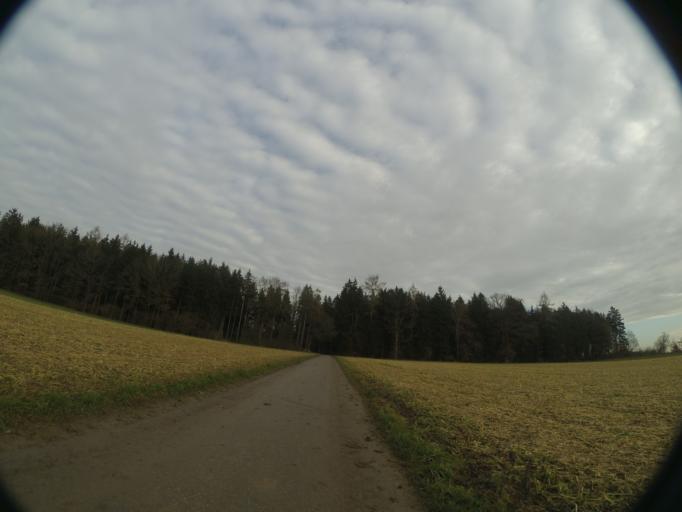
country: DE
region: Baden-Wuerttemberg
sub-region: Tuebingen Region
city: Erbach
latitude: 48.3623
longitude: 9.9241
